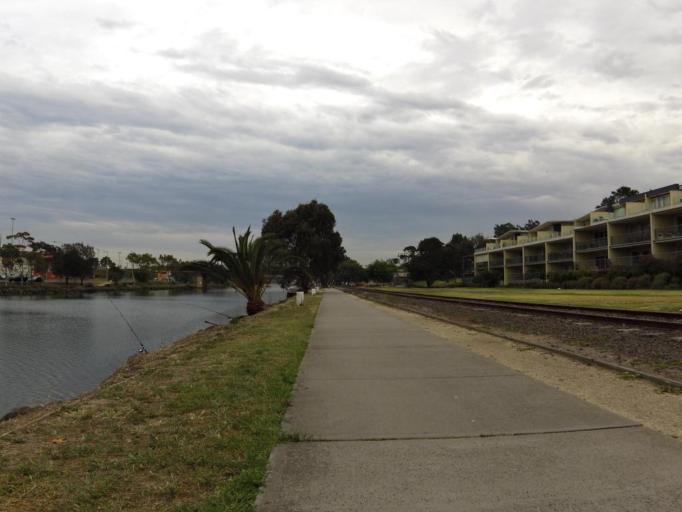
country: AU
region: Victoria
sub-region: Maribyrnong
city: Footscray
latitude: -37.8022
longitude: 144.9090
